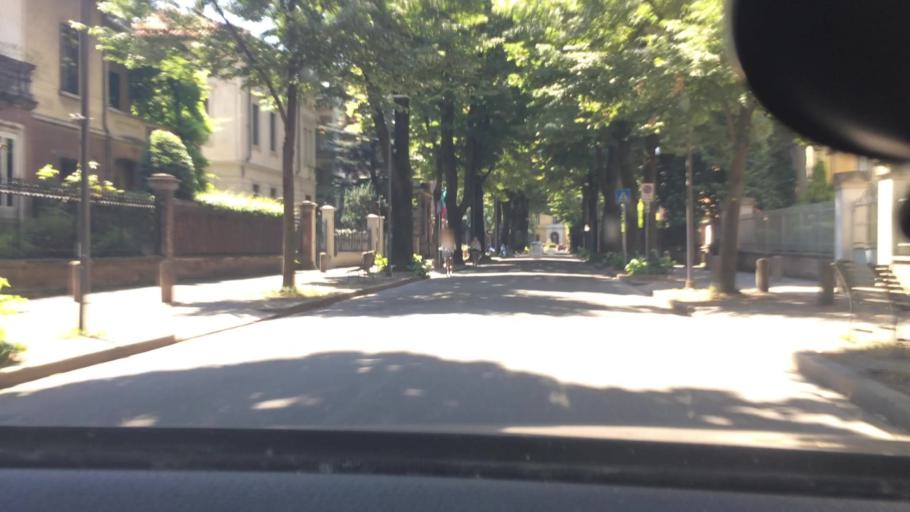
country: IT
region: Emilia-Romagna
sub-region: Provincia di Piacenza
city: Piacenza
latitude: 45.0499
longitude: 9.6864
